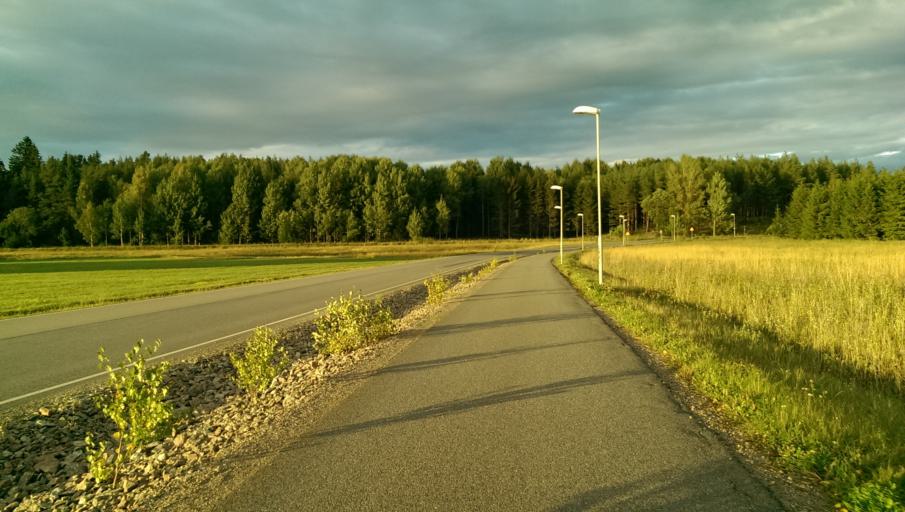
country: SE
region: OEstergoetland
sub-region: Linkopings Kommun
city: Linkoping
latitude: 58.3926
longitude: 15.5955
